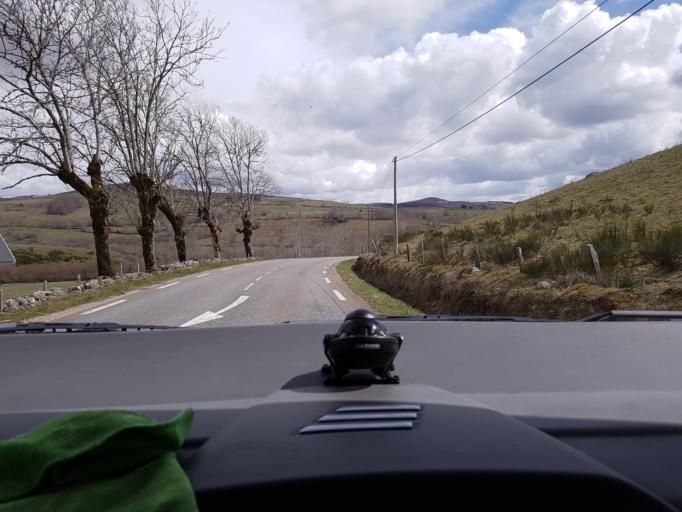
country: FR
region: Midi-Pyrenees
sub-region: Departement de l'Aveyron
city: Laguiole
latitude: 44.7038
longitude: 2.8602
